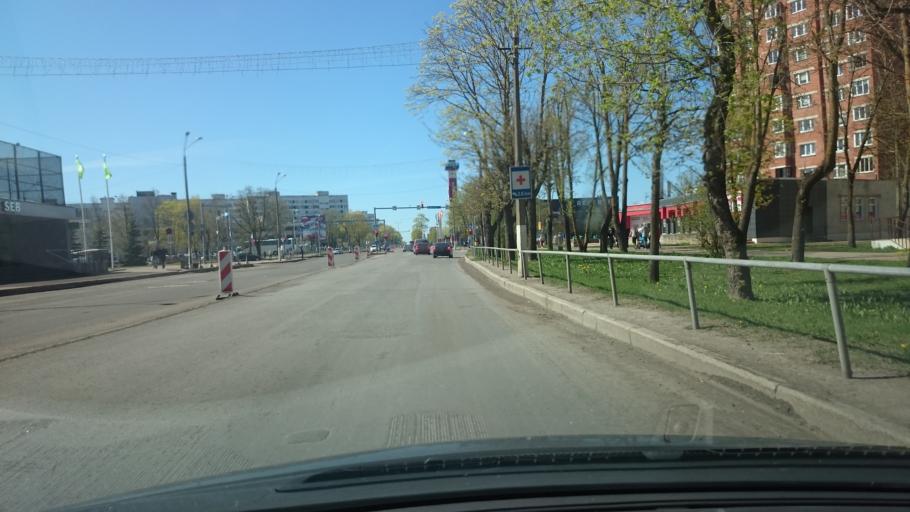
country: EE
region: Ida-Virumaa
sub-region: Narva linn
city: Narva
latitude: 59.3793
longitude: 28.1813
